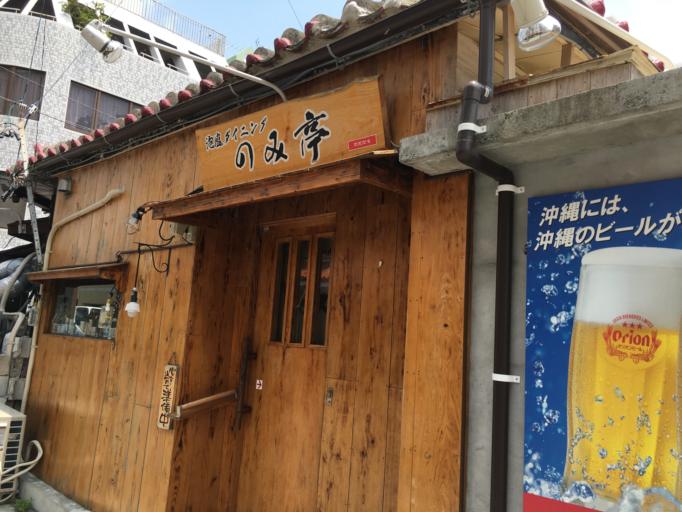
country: JP
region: Okinawa
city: Naha-shi
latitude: 26.2175
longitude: 127.6744
